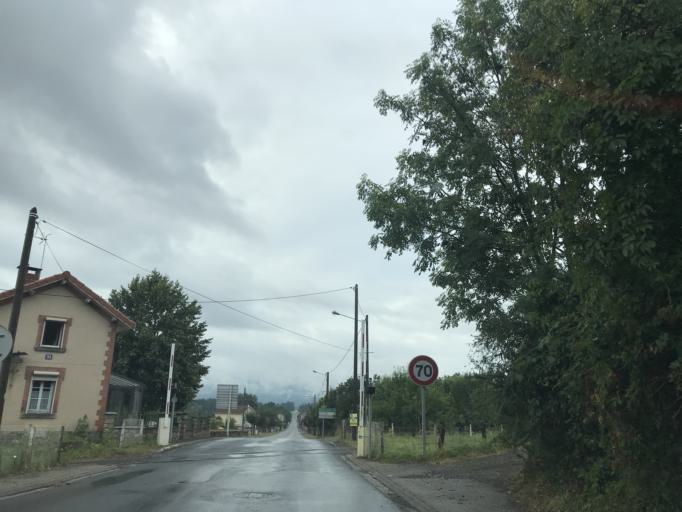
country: FR
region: Auvergne
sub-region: Departement du Puy-de-Dome
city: Arlanc
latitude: 45.4086
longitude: 3.7268
